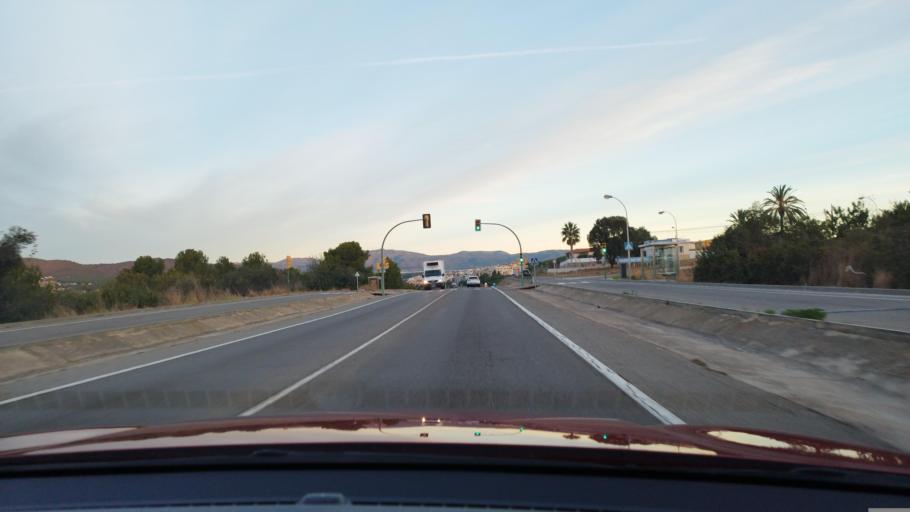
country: ES
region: Catalonia
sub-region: Provincia de Tarragona
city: El Vendrell
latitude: 41.2130
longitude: 1.5471
